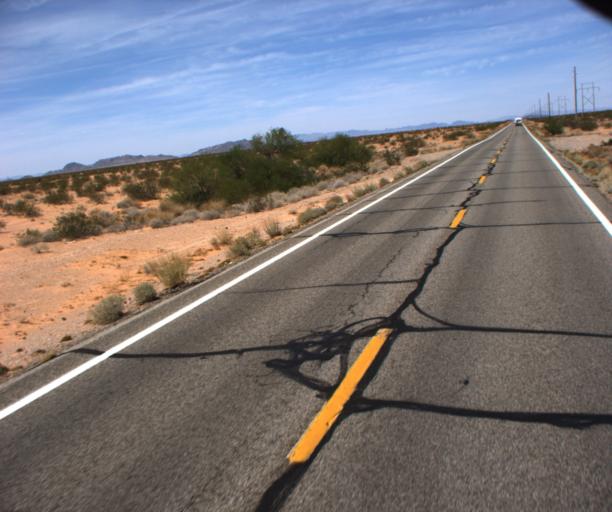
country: US
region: Arizona
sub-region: La Paz County
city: Quartzsite
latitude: 33.8705
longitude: -114.2169
